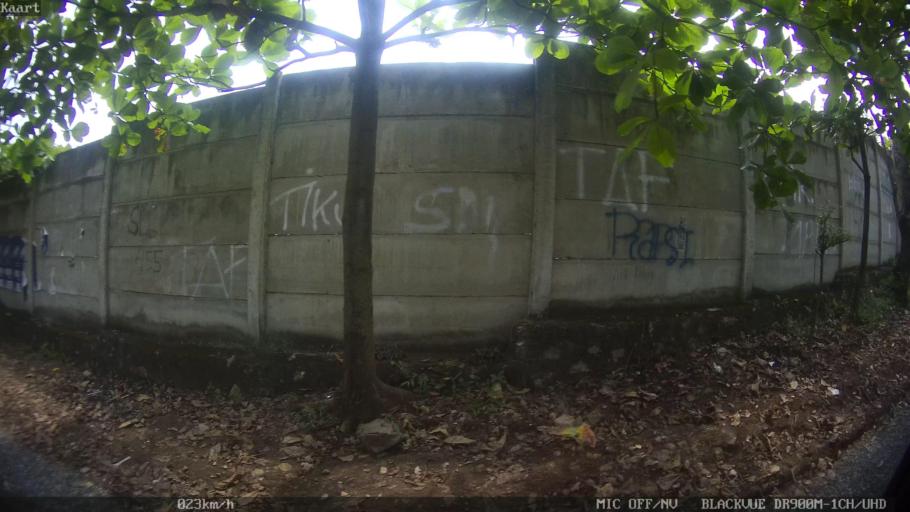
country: ID
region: Lampung
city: Bandarlampung
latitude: -5.4331
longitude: 105.2657
